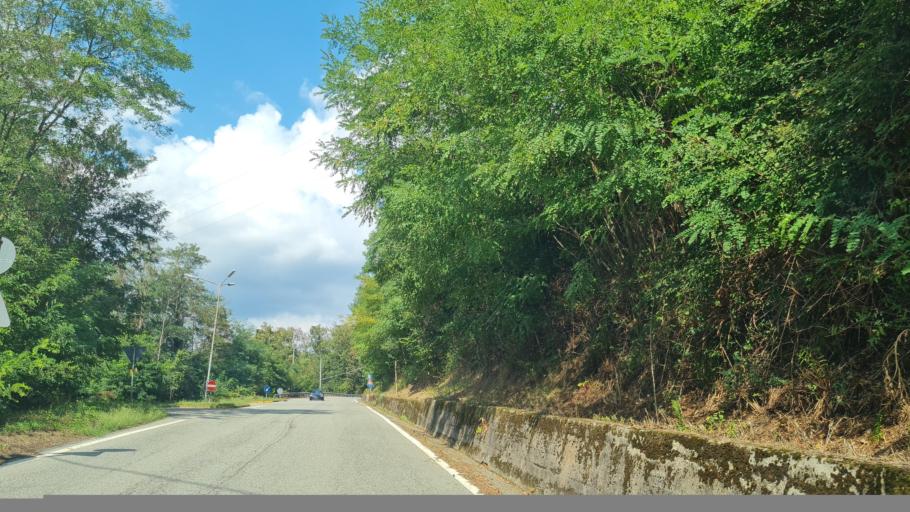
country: IT
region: Piedmont
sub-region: Provincia di Biella
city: Fontanella-Ozino
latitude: 45.6178
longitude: 8.1647
